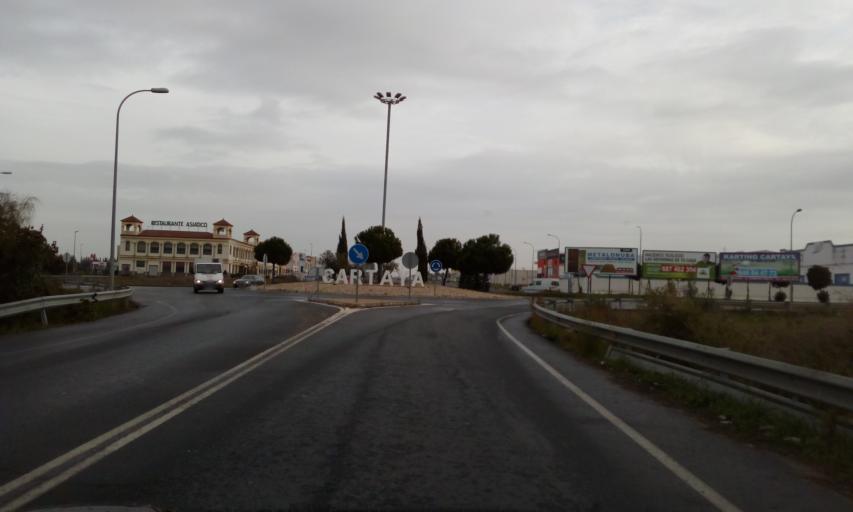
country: ES
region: Andalusia
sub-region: Provincia de Huelva
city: Cartaya
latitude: 37.2845
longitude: -7.1731
